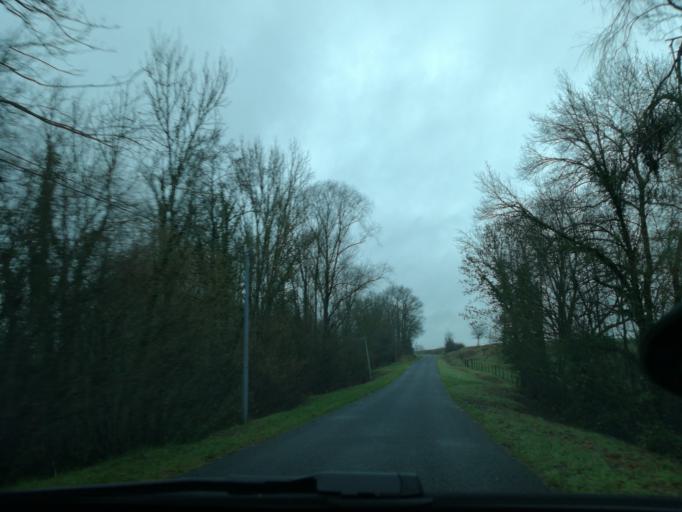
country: FR
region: Lorraine
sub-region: Departement de la Meuse
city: Revigny-sur-Ornain
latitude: 48.8391
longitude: 5.0460
